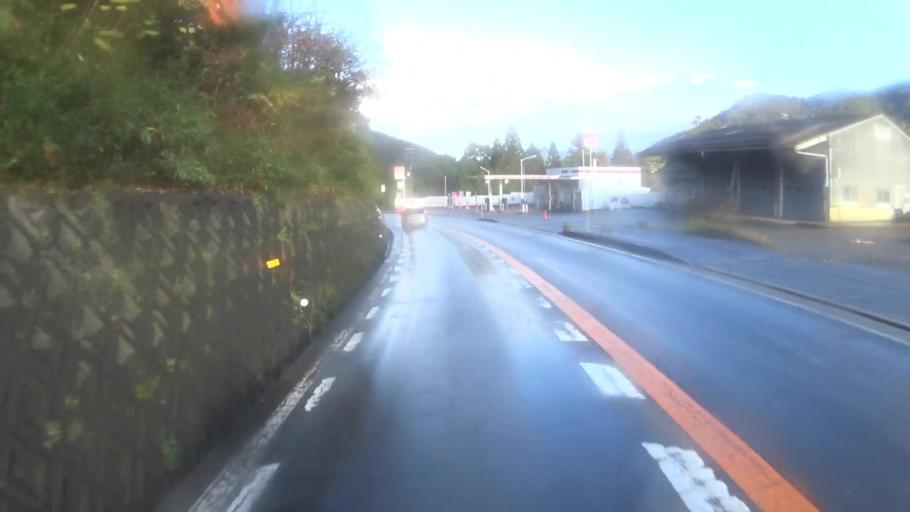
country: JP
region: Kyoto
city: Ayabe
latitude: 35.2304
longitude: 135.2243
